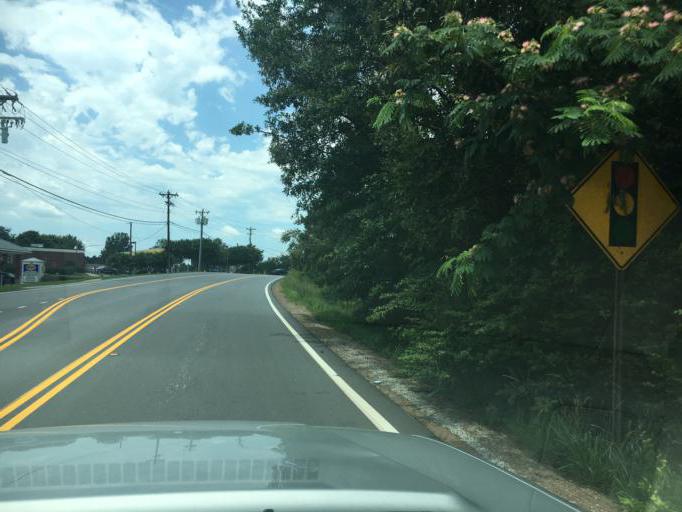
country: US
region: South Carolina
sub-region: Greenville County
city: Taylors
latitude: 34.8714
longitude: -82.2523
